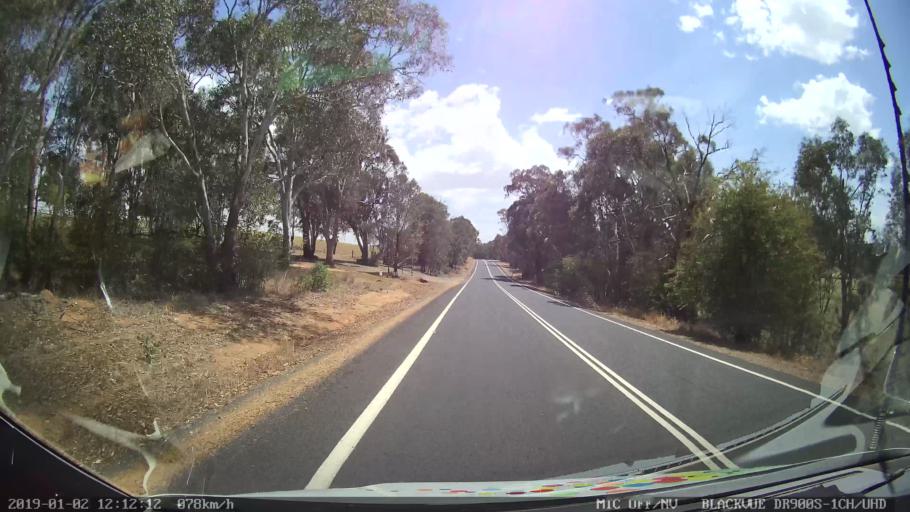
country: AU
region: New South Wales
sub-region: Young
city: Young
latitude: -34.4397
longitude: 148.2550
